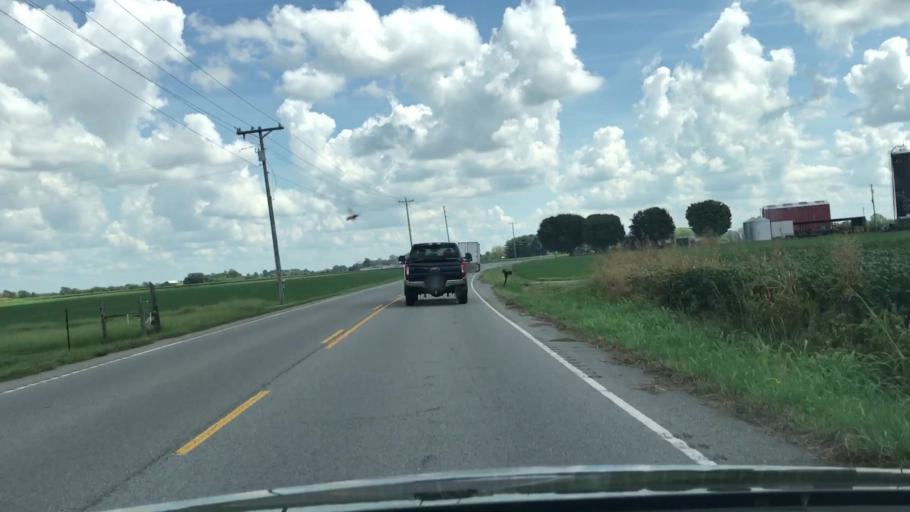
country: US
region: Tennessee
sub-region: Robertson County
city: Cross Plains
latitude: 36.5554
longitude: -86.7925
